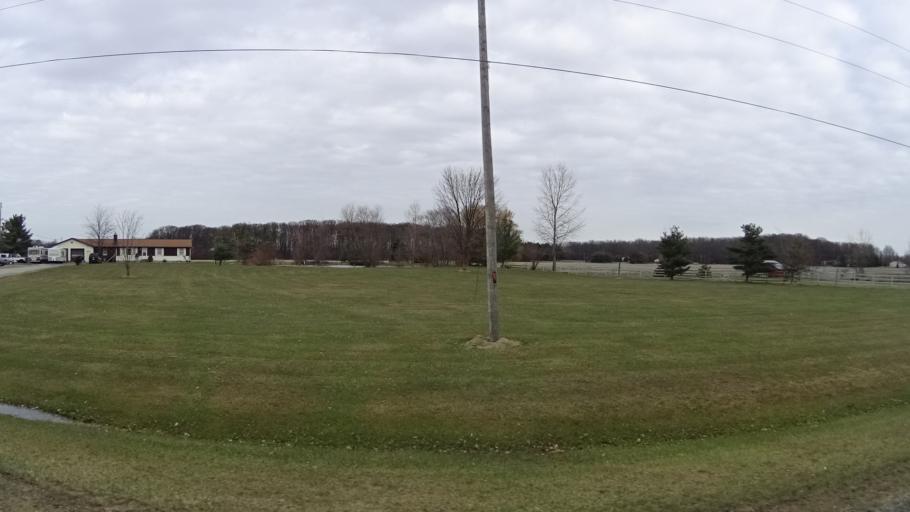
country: US
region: Ohio
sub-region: Lorain County
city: Camden
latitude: 41.1730
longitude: -82.3386
